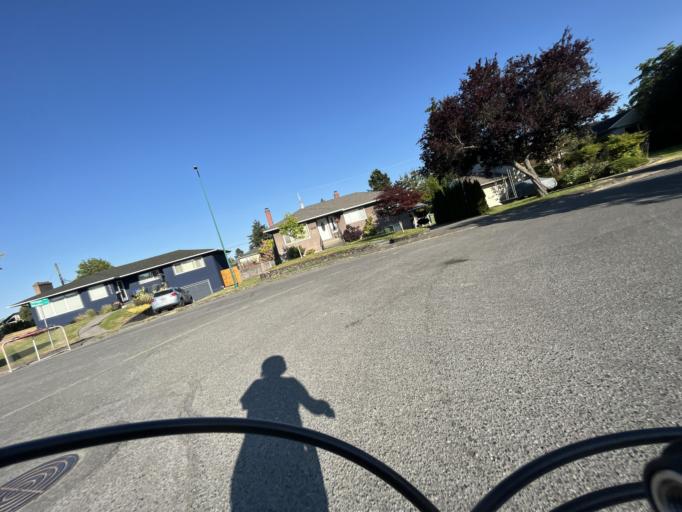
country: CA
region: British Columbia
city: Oak Bay
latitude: 48.4376
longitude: -123.3176
